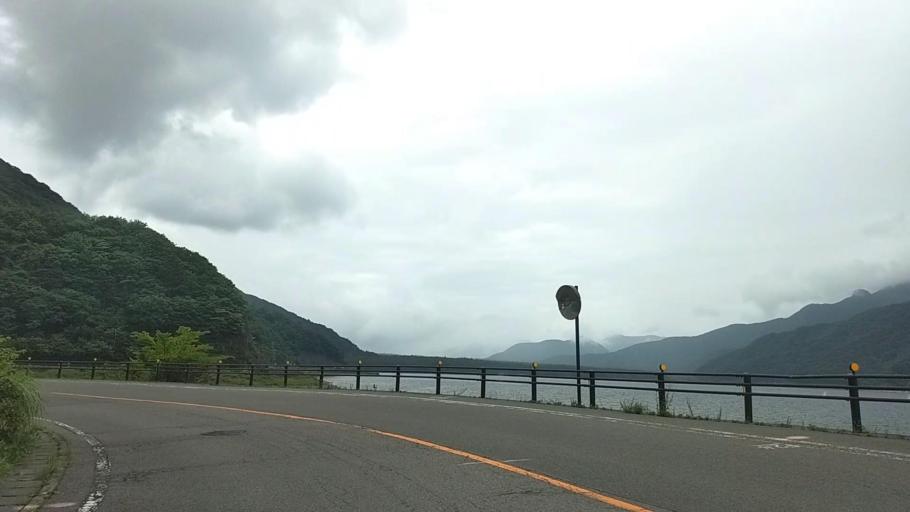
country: JP
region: Yamanashi
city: Fujikawaguchiko
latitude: 35.4987
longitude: 138.6970
